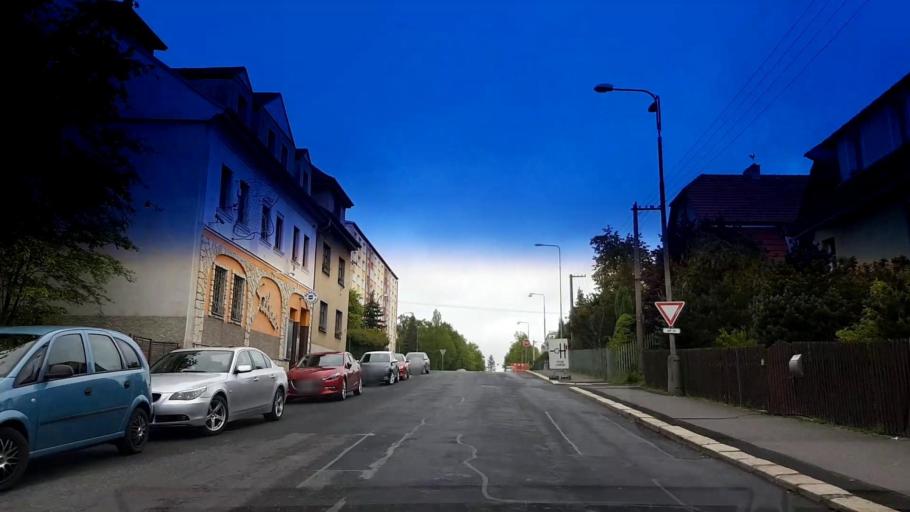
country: CZ
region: Karlovarsky
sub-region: Okres Cheb
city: Cheb
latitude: 50.0681
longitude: 12.3708
